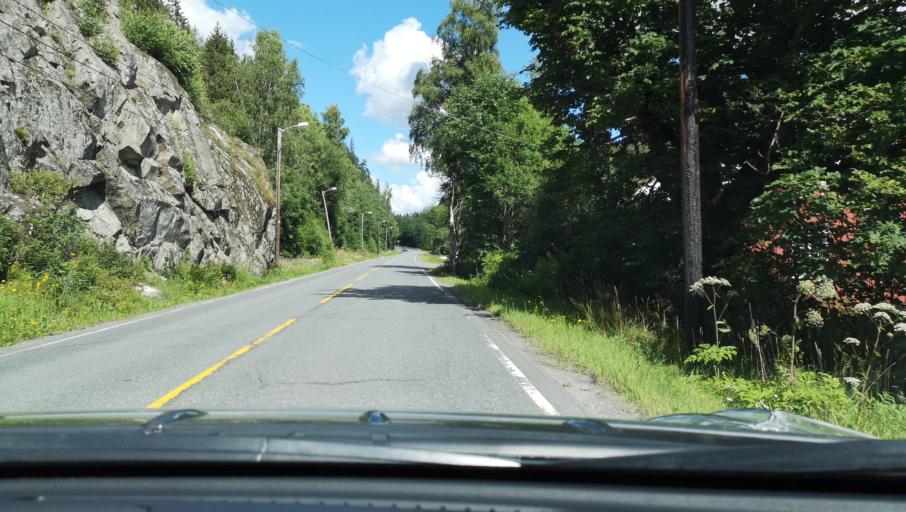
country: NO
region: Ostfold
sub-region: Hobol
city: Tomter
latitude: 59.6515
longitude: 10.9956
